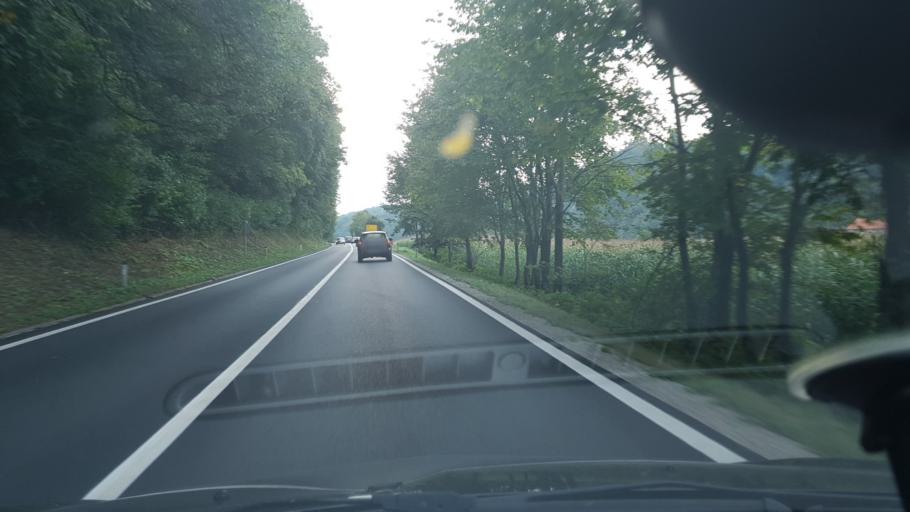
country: SI
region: Krsko
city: Krsko
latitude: 45.9847
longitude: 15.4704
